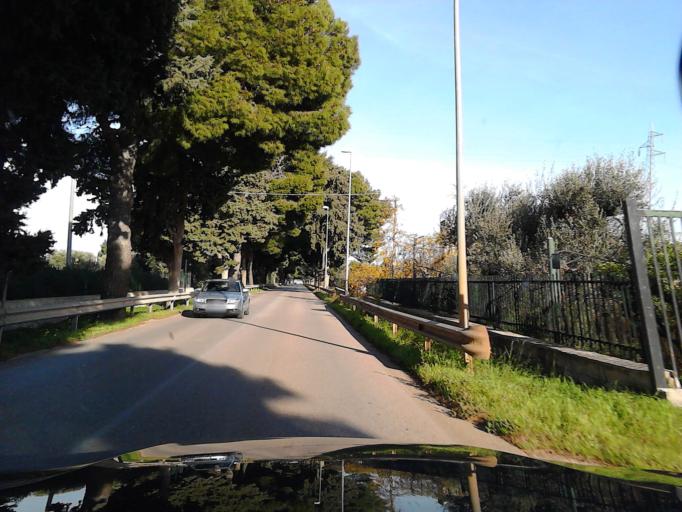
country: IT
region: Apulia
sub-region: Provincia di Bari
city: Mola di Bari
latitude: 41.0460
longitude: 17.0661
